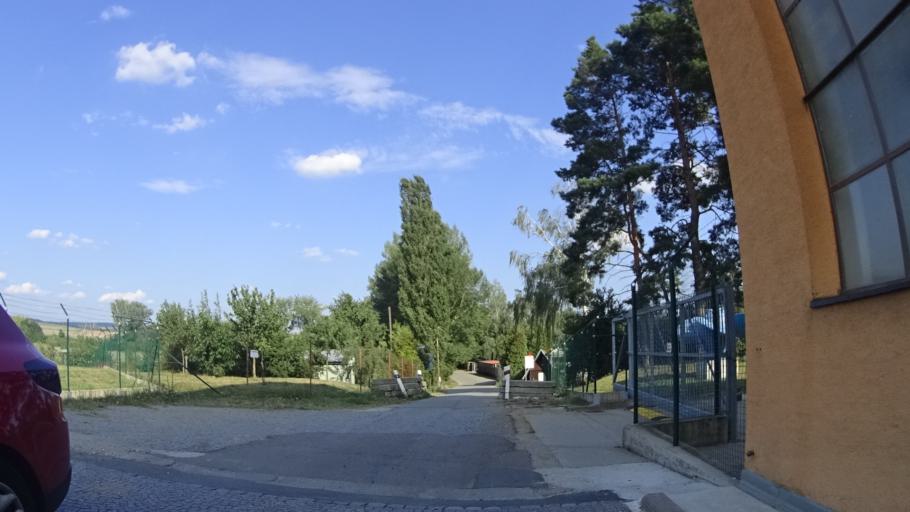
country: CZ
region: Zlin
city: Spytihnev
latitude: 49.1351
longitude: 17.5034
